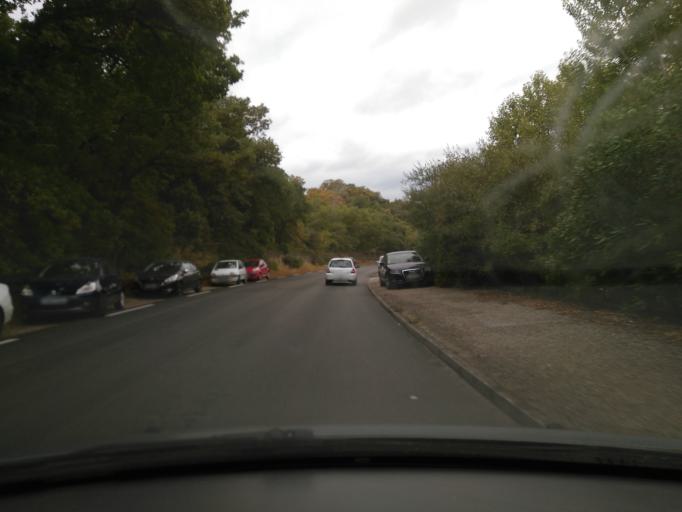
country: FR
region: Rhone-Alpes
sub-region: Departement de la Drome
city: Grignan
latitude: 44.4154
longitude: 4.9069
